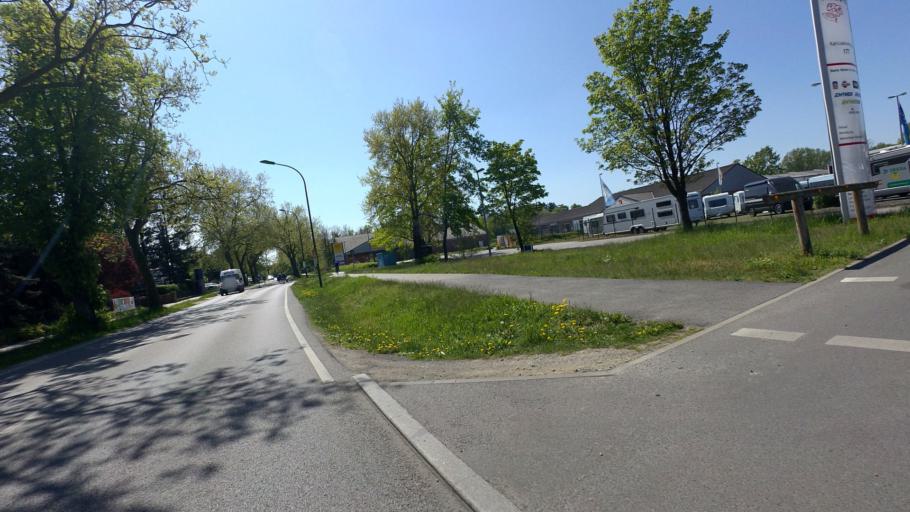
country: DE
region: Brandenburg
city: Konigs Wusterhausen
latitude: 52.2745
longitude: 13.6323
